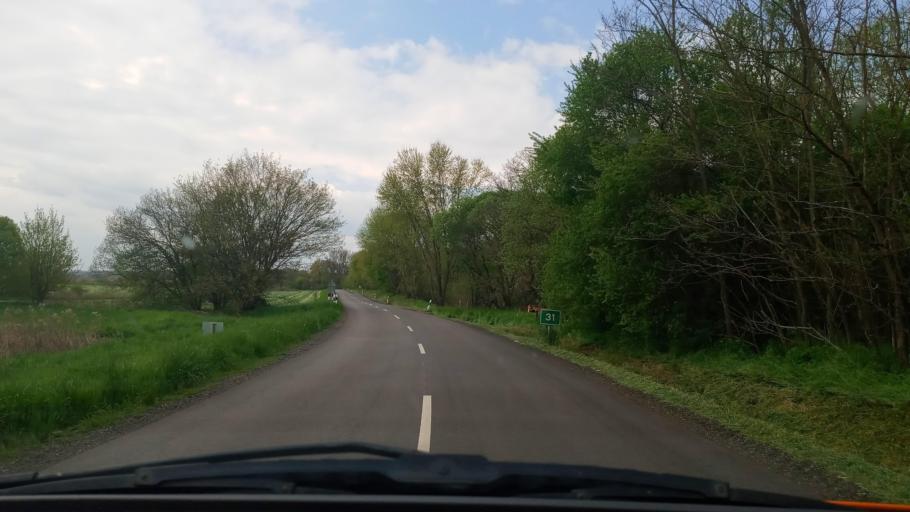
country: HU
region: Baranya
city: Sasd
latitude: 46.2682
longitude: 18.0757
